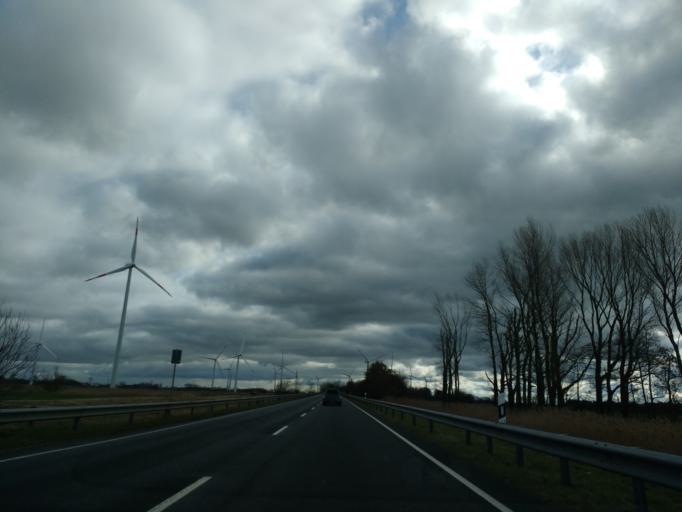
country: DE
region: Lower Saxony
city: Cuxhaven
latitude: 53.8210
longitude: 8.6956
